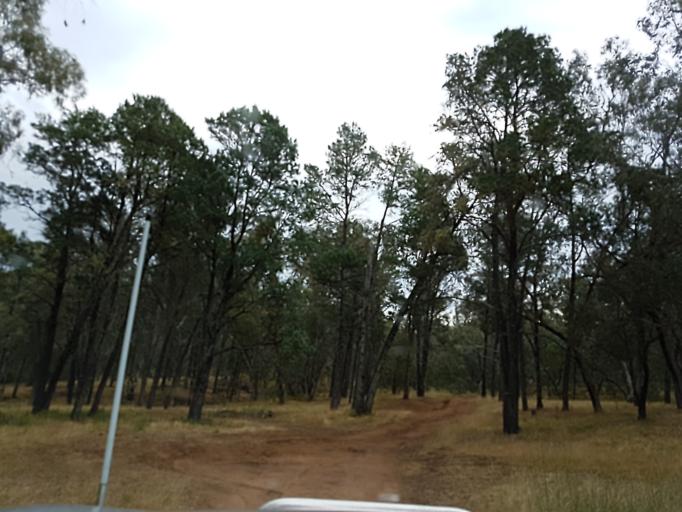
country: AU
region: New South Wales
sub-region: Snowy River
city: Jindabyne
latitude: -36.9416
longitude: 148.3959
